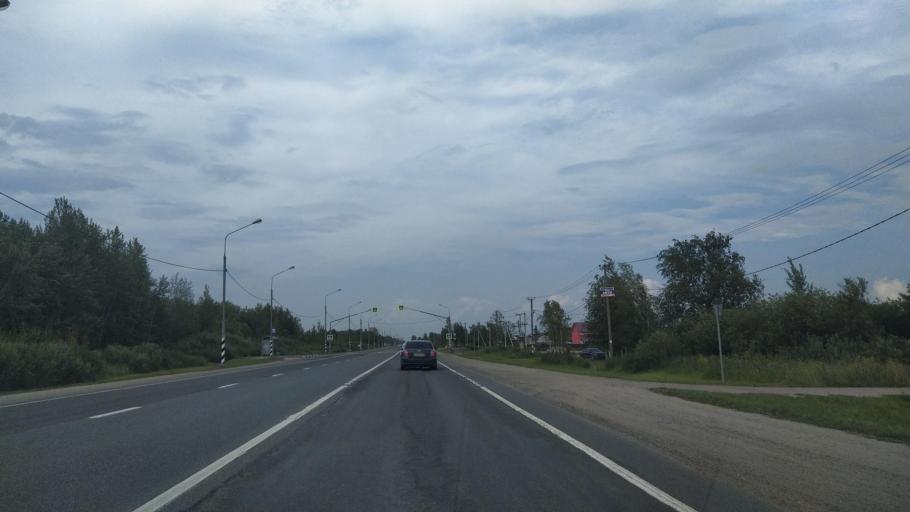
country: RU
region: Novgorod
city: Pankovka
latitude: 58.4803
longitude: 31.1846
